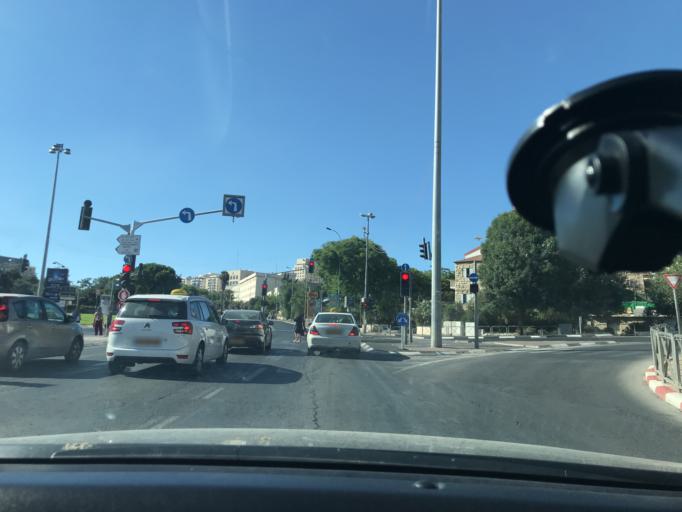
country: IL
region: Jerusalem
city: West Jerusalem
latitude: 31.7825
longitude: 35.2085
